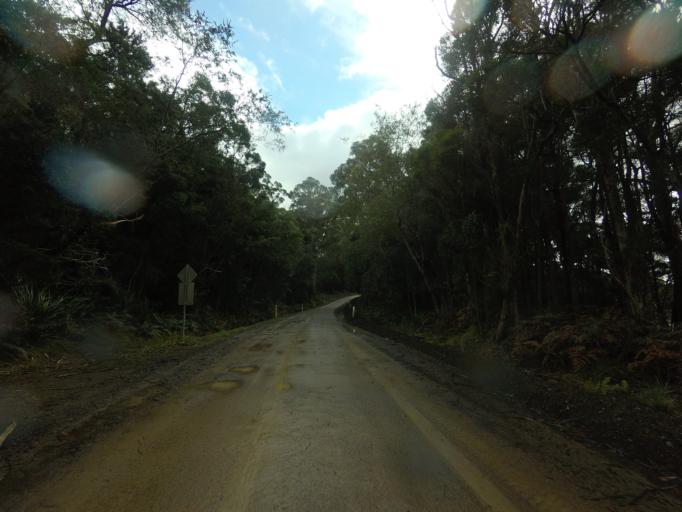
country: AU
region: Tasmania
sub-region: Huon Valley
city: Geeveston
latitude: -43.5771
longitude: 146.8872
